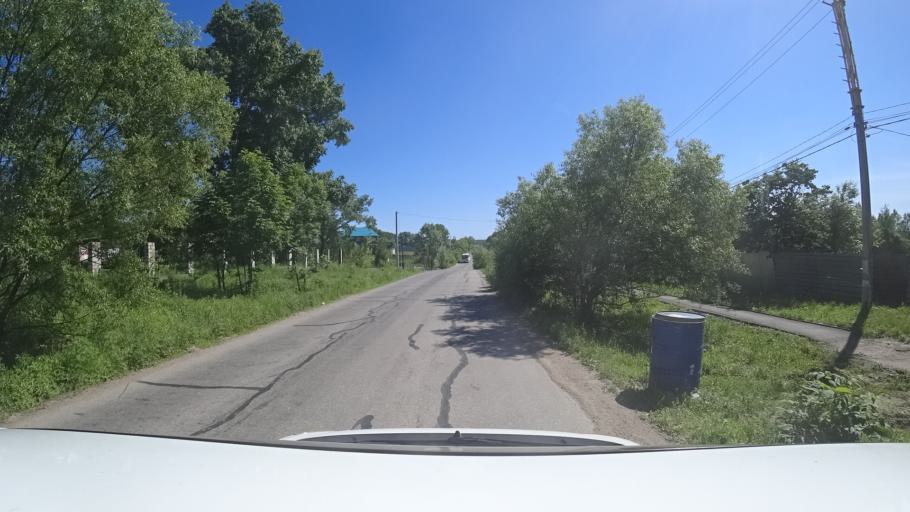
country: RU
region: Khabarovsk Krai
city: Topolevo
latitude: 48.5552
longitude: 135.1914
